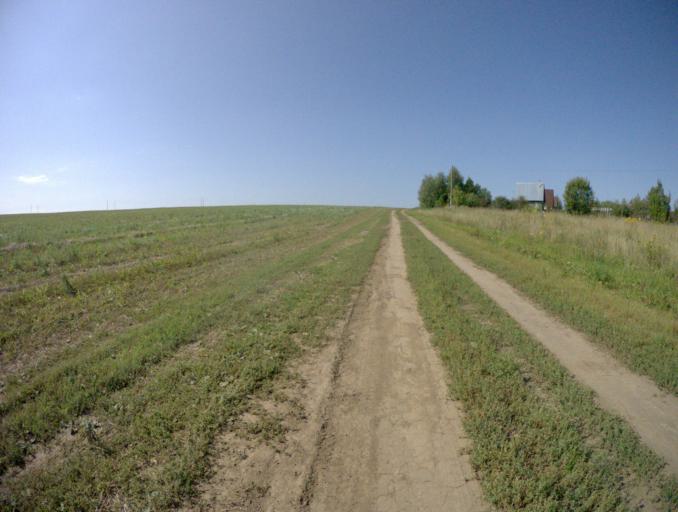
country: RU
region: Vladimir
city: Vladimir
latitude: 56.2505
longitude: 40.4145
